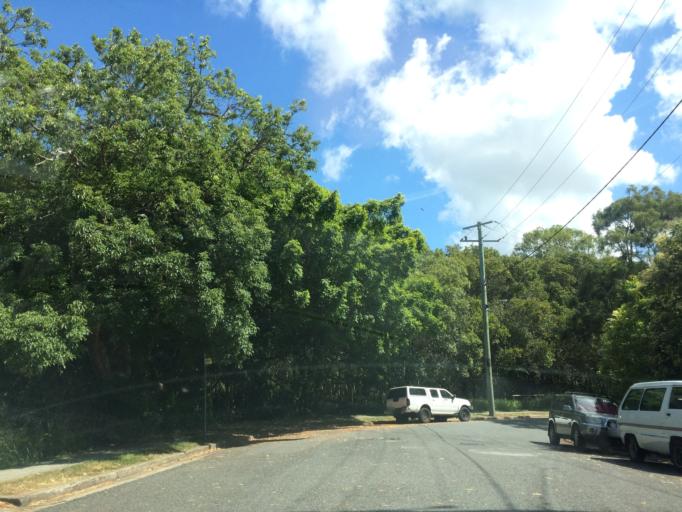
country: AU
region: Queensland
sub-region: Brisbane
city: Woolloongabba
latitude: -27.4905
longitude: 153.0460
